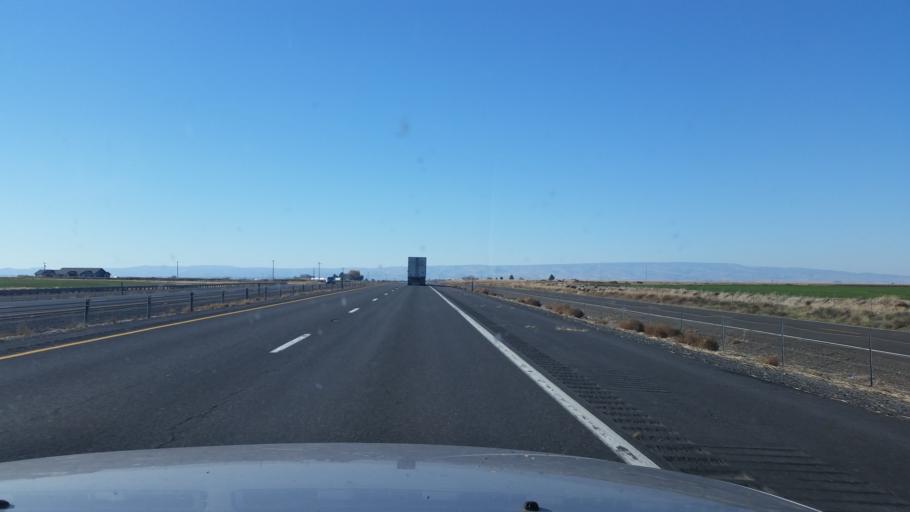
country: US
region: Washington
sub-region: Grant County
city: Quincy
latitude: 47.1036
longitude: -119.7848
